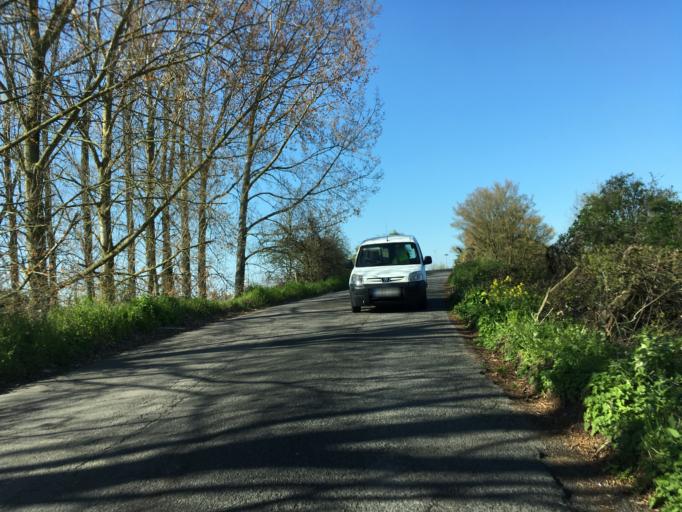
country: GB
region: England
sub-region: North Somerset
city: Easton-in-Gordano
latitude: 51.4813
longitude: -2.7062
